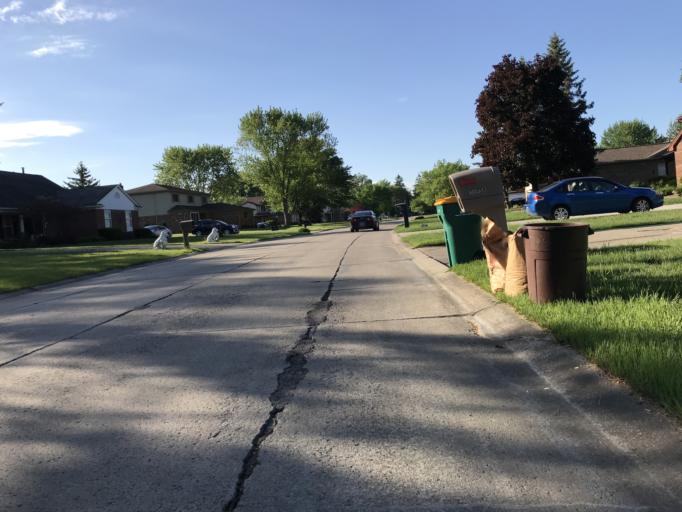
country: US
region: Michigan
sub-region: Oakland County
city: Farmington
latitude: 42.4683
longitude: -83.3272
